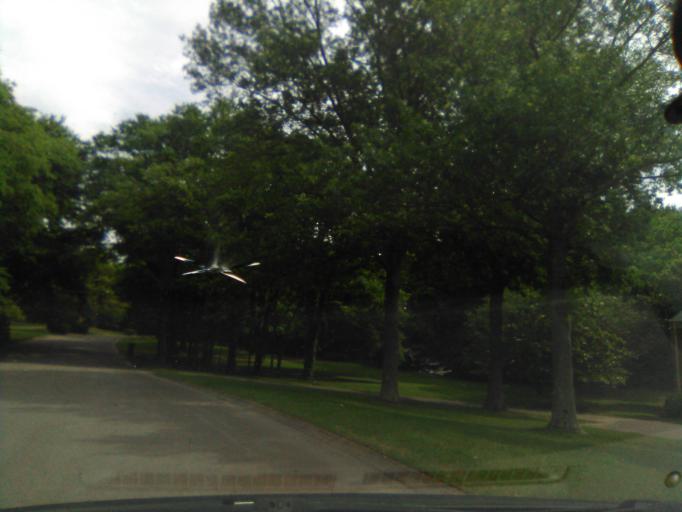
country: US
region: Tennessee
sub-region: Davidson County
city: Belle Meade
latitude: 36.0993
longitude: -86.8817
